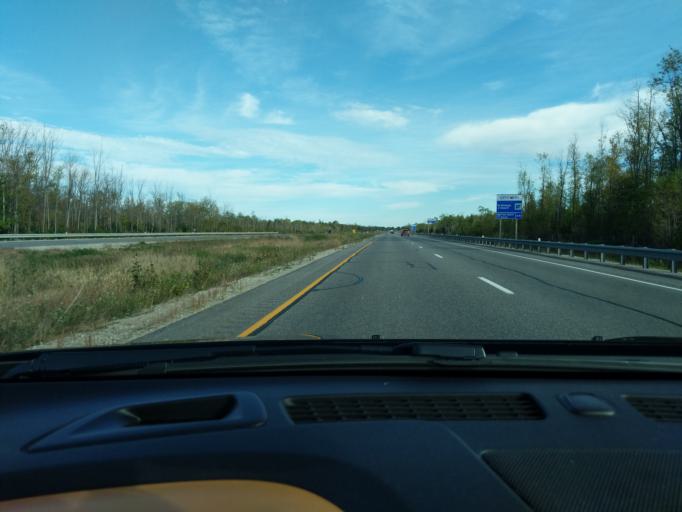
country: CA
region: Ontario
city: Collingwood
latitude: 44.4666
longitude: -80.1299
